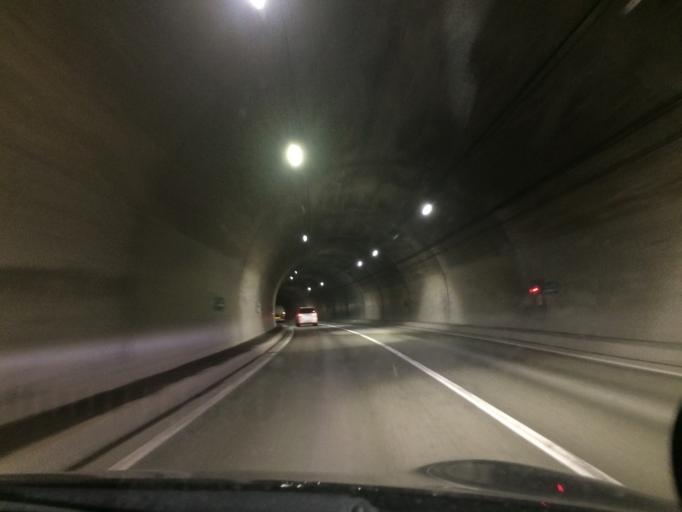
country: JP
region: Hokkaido
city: Shimo-furano
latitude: 42.9604
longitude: 142.6162
